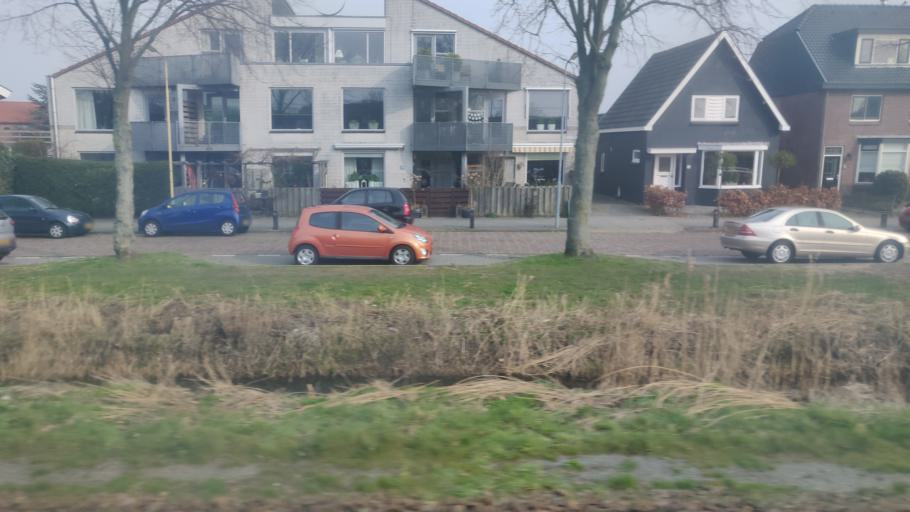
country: NL
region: North Holland
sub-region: Gemeente Castricum
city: Castricum
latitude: 52.5432
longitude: 4.6621
